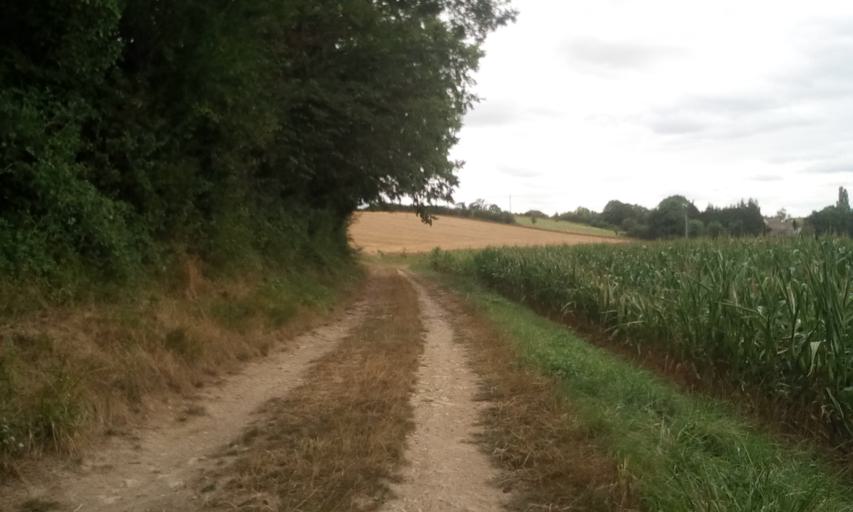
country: FR
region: Lower Normandy
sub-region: Departement du Calvados
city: Bellengreville
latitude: 49.1102
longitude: -0.1976
